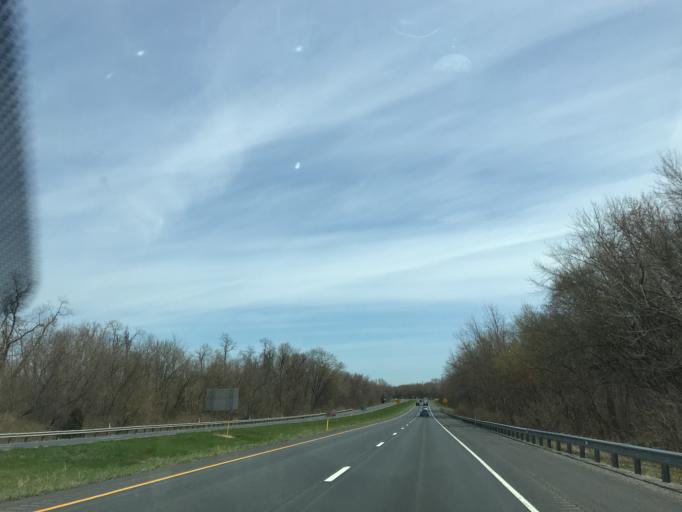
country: US
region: Pennsylvania
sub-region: Snyder County
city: Selinsgrove
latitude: 40.8039
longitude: -76.8544
